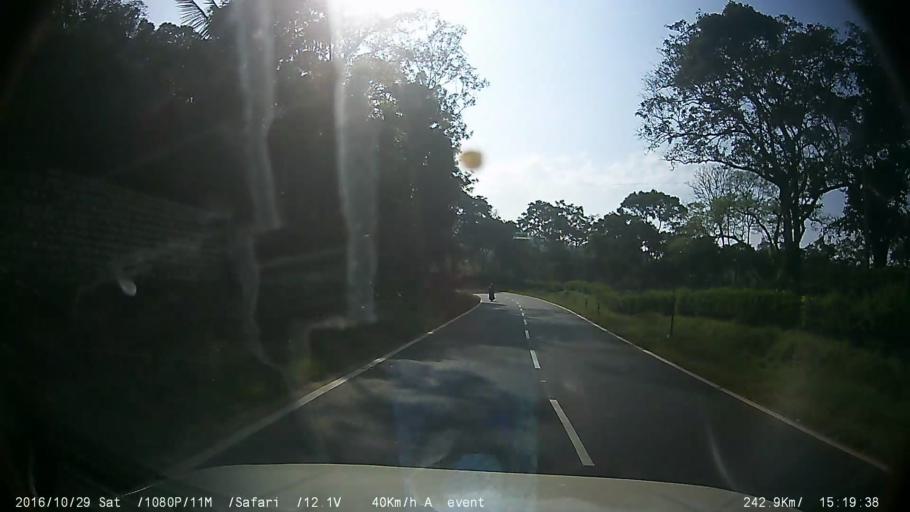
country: IN
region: Karnataka
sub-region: Kodagu
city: Suntikoppa
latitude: 12.4346
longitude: 75.7870
